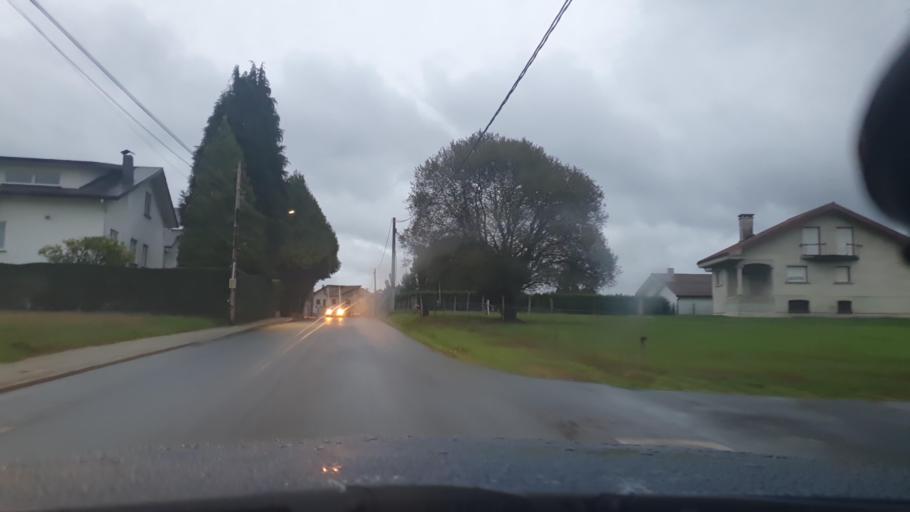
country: ES
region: Galicia
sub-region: Provincia da Coruna
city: Santiago de Compostela
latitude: 42.8485
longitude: -8.5885
